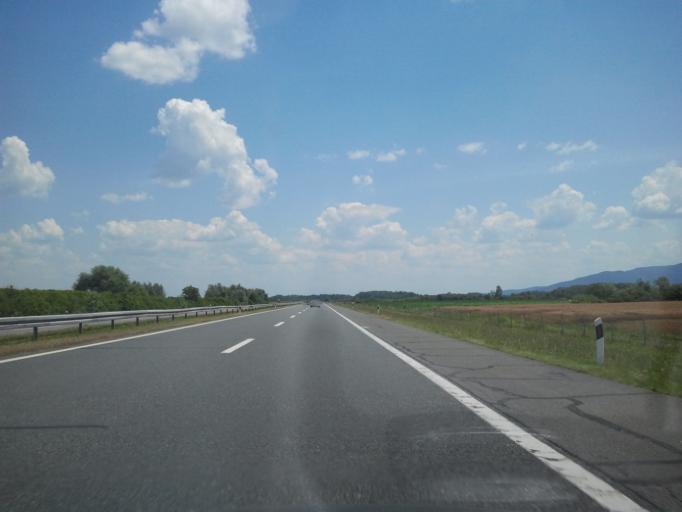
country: HR
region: Brodsko-Posavska
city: Vrbova
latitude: 45.1976
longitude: 17.5819
